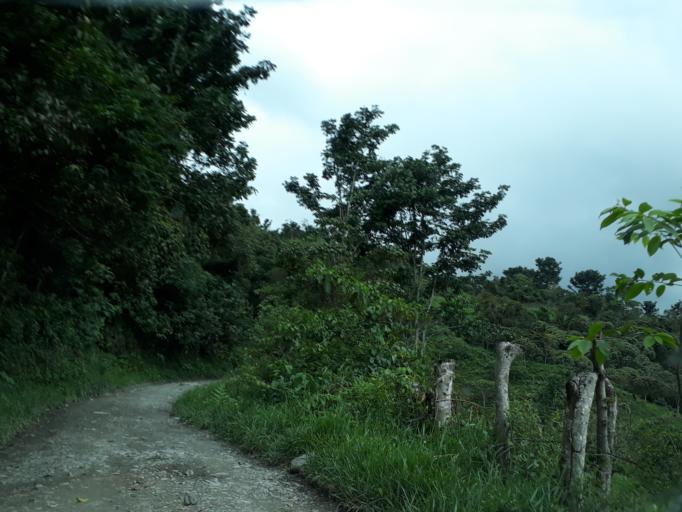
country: CO
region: Boyaca
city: Muzo
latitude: 5.3823
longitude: -74.0927
